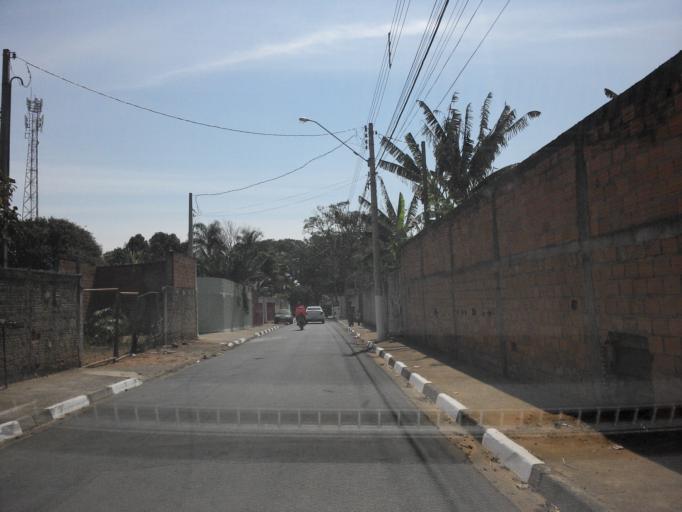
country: BR
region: Sao Paulo
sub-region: Hortolandia
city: Hortolandia
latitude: -22.8984
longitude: -47.2279
